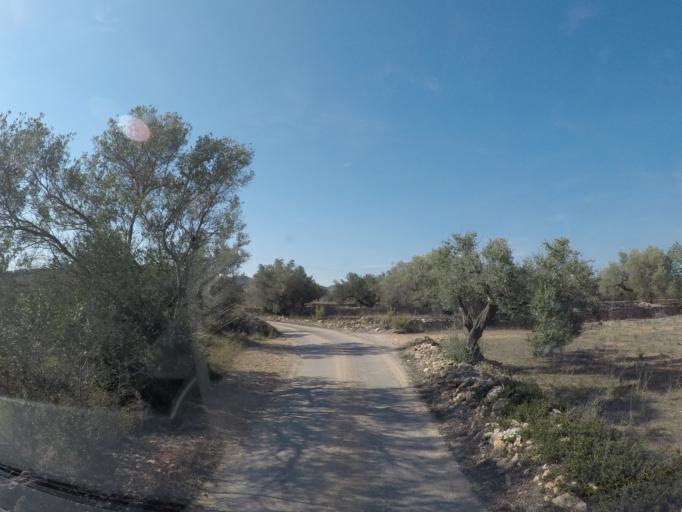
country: ES
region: Catalonia
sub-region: Provincia de Tarragona
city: El Perello
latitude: 40.9013
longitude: 0.7301
